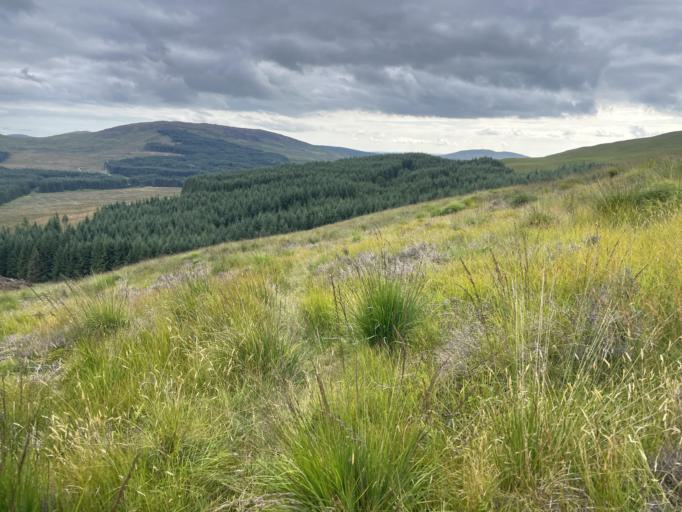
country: GB
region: Scotland
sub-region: Dumfries and Galloway
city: Newton Stewart
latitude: 54.9491
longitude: -4.2844
